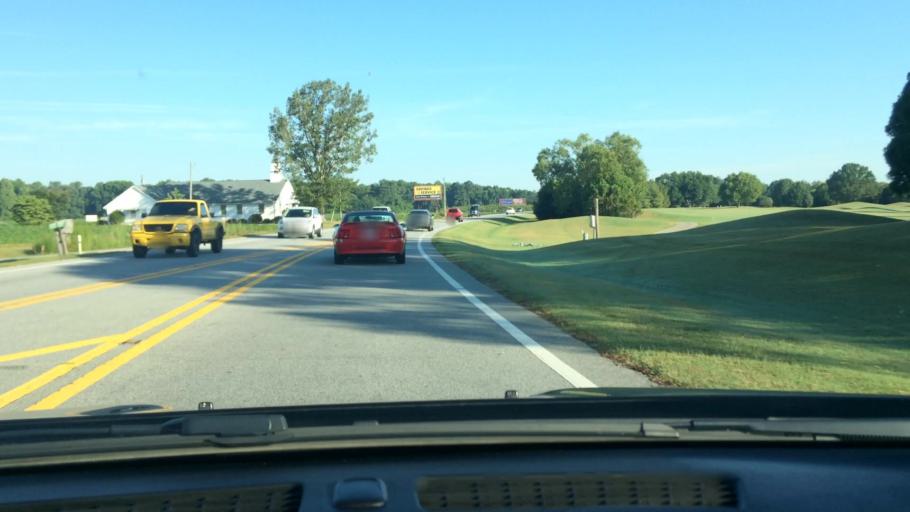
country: US
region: North Carolina
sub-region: Pitt County
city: Summerfield
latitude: 35.6350
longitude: -77.4486
